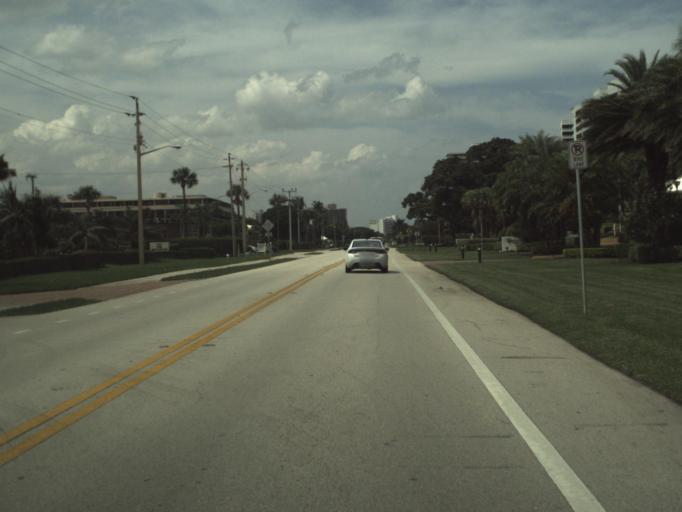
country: US
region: Florida
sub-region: Broward County
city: Deerfield Beach
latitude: 26.3277
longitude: -80.0750
